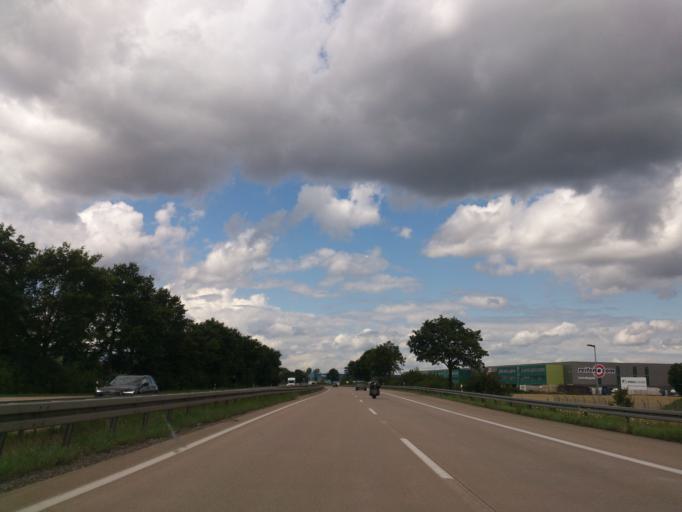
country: DE
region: Lower Saxony
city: Langenhagen
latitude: 52.4453
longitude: 9.7036
